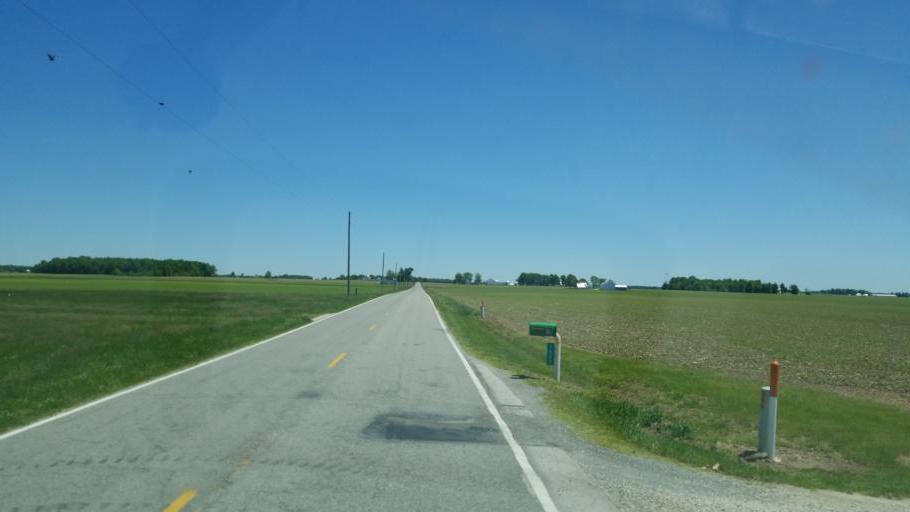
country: US
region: Ohio
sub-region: Darke County
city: Union City
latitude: 40.2814
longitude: -84.7434
